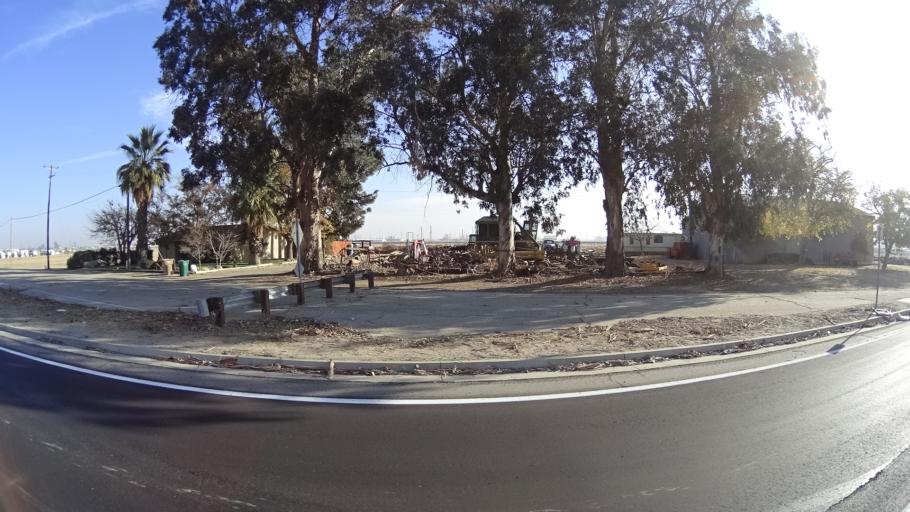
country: US
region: California
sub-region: Kern County
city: Greenacres
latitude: 35.3720
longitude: -119.0924
